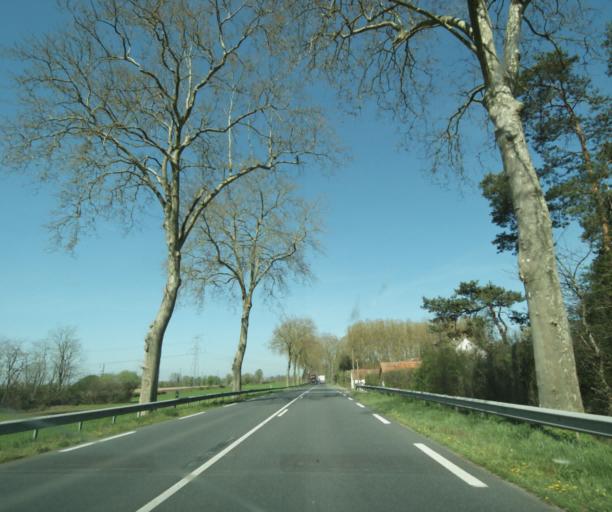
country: FR
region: Bourgogne
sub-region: Departement de la Nievre
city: Chantenay-Saint-Imbert
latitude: 46.6887
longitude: 3.2182
